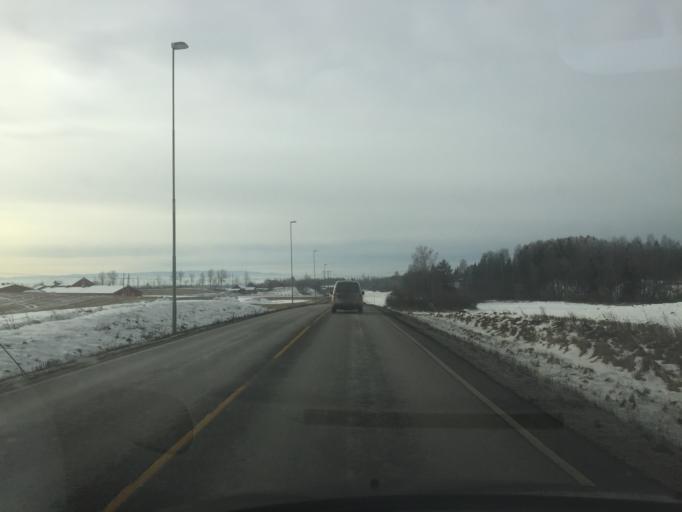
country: NO
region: Hedmark
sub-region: Loten
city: Loten
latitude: 60.8089
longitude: 11.3030
